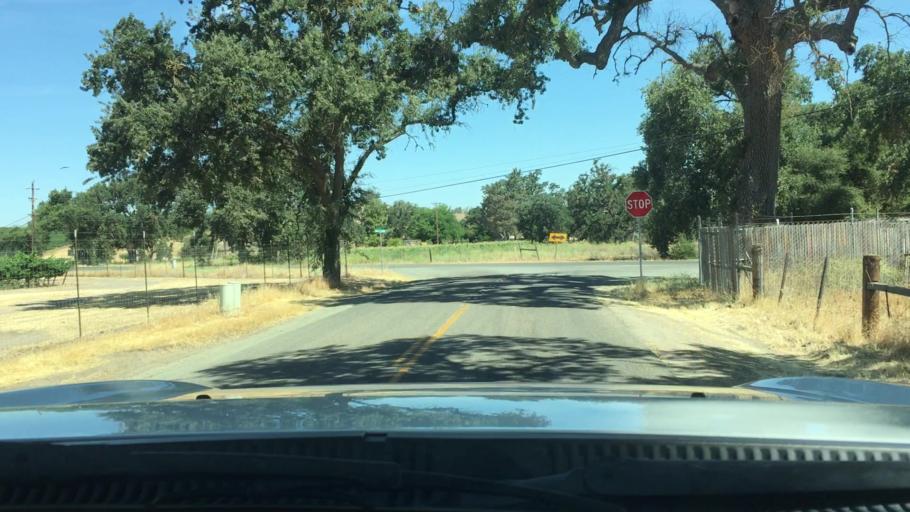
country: US
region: California
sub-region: San Luis Obispo County
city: Paso Robles
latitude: 35.5734
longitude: -120.6084
